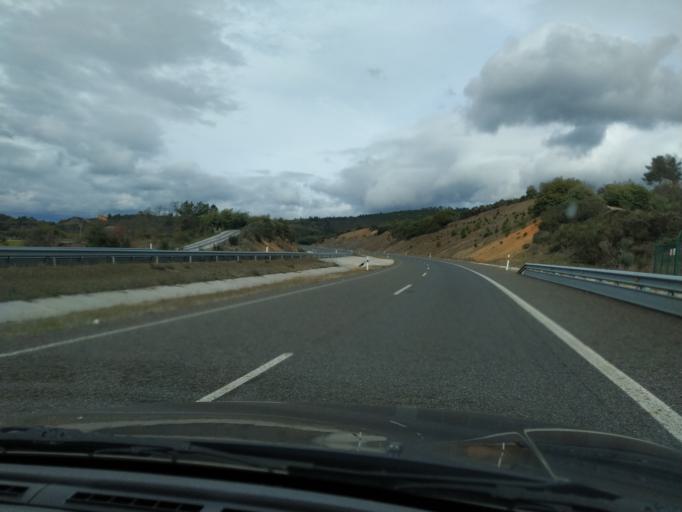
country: ES
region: Galicia
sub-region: Provincia de Ourense
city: Oimbra
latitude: 41.8473
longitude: -7.4122
